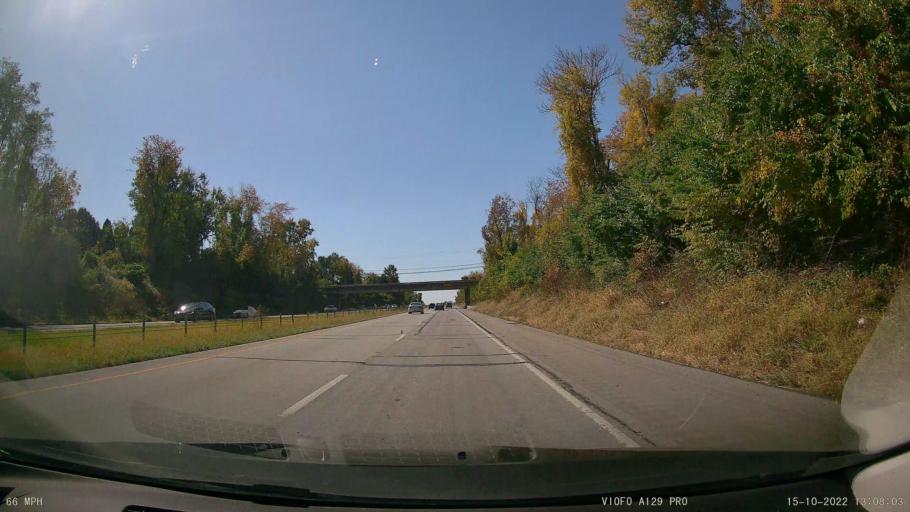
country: US
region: Pennsylvania
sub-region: Berks County
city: Fox Chase
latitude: 40.4020
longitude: -75.9578
